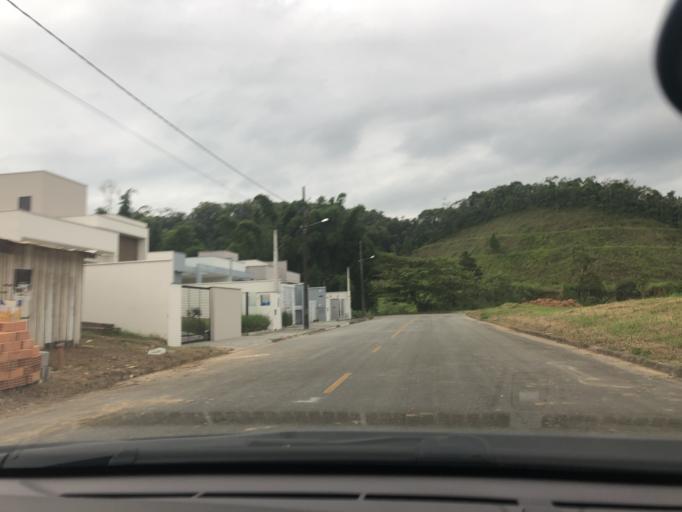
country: BR
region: Santa Catarina
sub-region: Jaragua Do Sul
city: Jaragua do Sul
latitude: -26.4999
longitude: -49.1406
